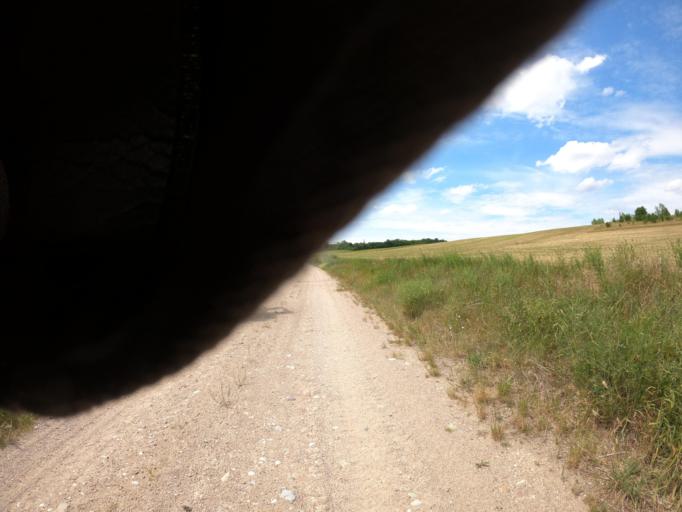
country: DE
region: Brandenburg
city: Letschin
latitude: 52.7333
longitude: 14.3927
